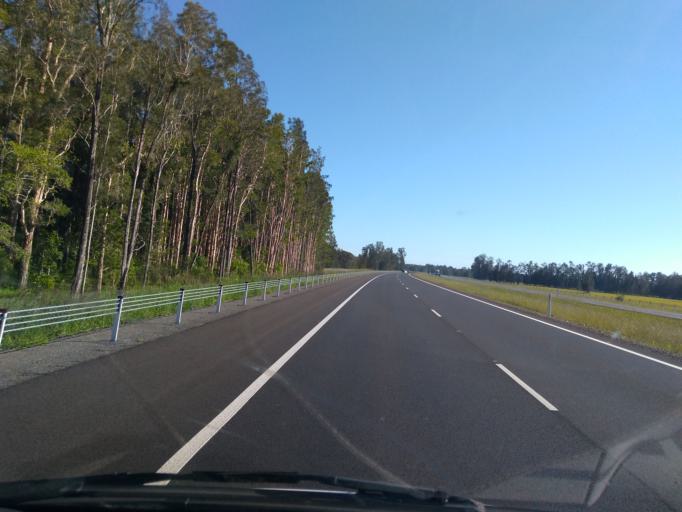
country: AU
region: New South Wales
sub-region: Port Macquarie-Hastings
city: North Shore
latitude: -31.3409
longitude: 152.8106
